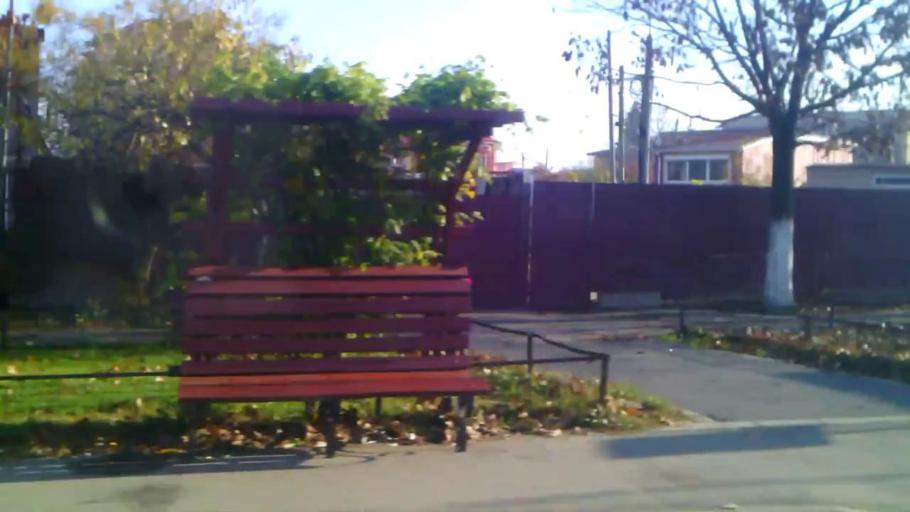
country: RO
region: Ilfov
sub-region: Comuna Popesti-Leordeni
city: Popesti-Leordeni
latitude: 44.3745
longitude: 26.1388
